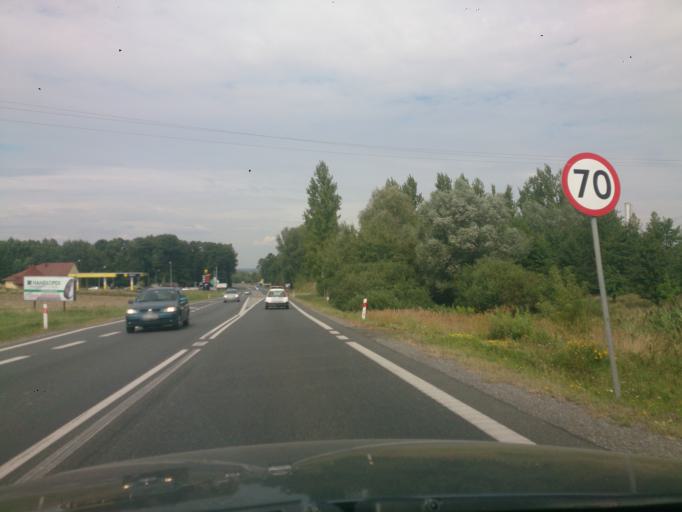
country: PL
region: Subcarpathian Voivodeship
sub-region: Powiat kolbuszowski
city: Kolbuszowa
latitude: 50.2068
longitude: 21.8291
